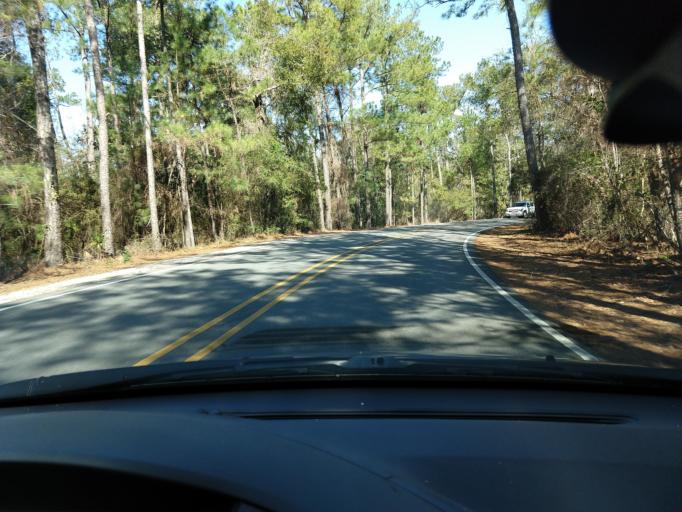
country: US
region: Mississippi
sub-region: Jackson County
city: Gulf Park Estates
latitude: 30.3954
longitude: -88.7881
